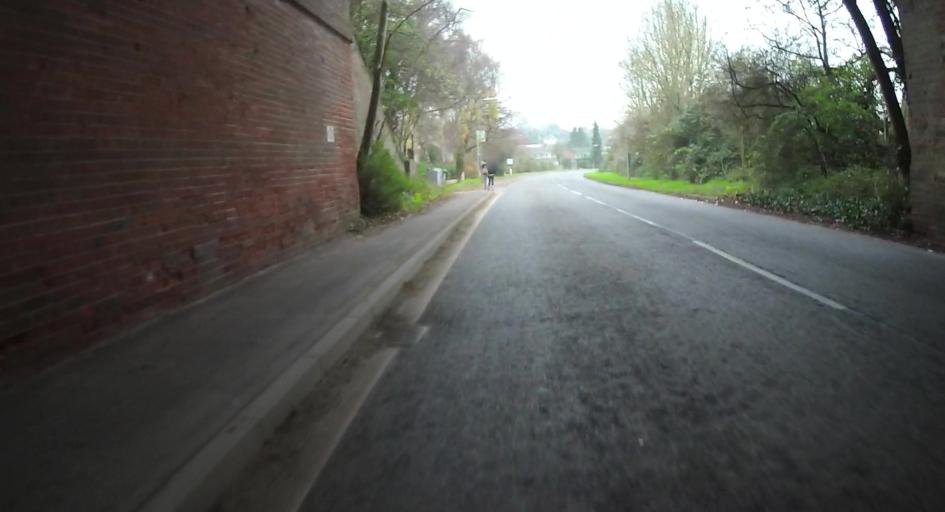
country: GB
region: England
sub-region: Hampshire
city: Kings Worthy
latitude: 51.0983
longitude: -1.3023
